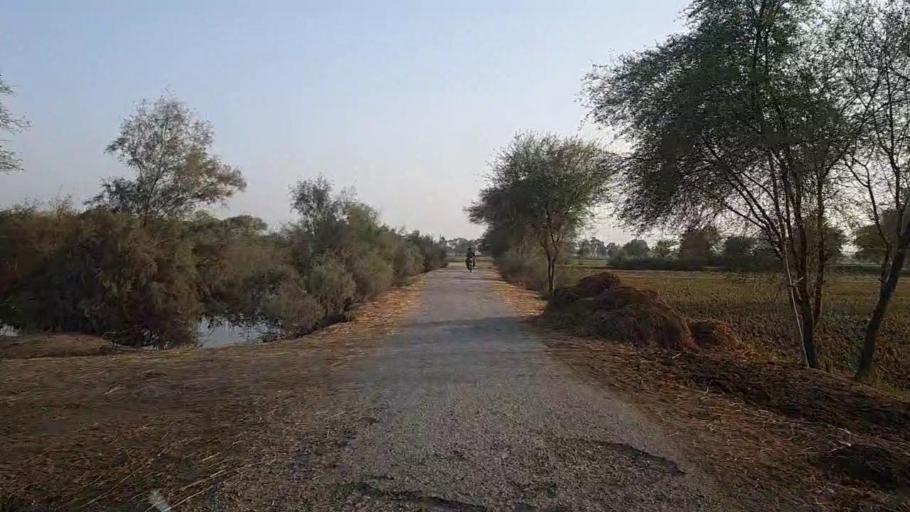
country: PK
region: Sindh
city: Kandhkot
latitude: 28.2364
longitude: 69.0911
